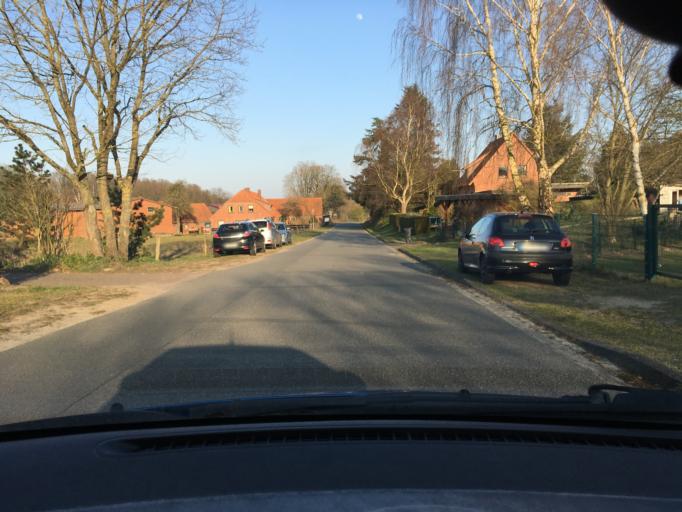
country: DE
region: Lower Saxony
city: Reinstorf
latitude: 53.2413
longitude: 10.5896
